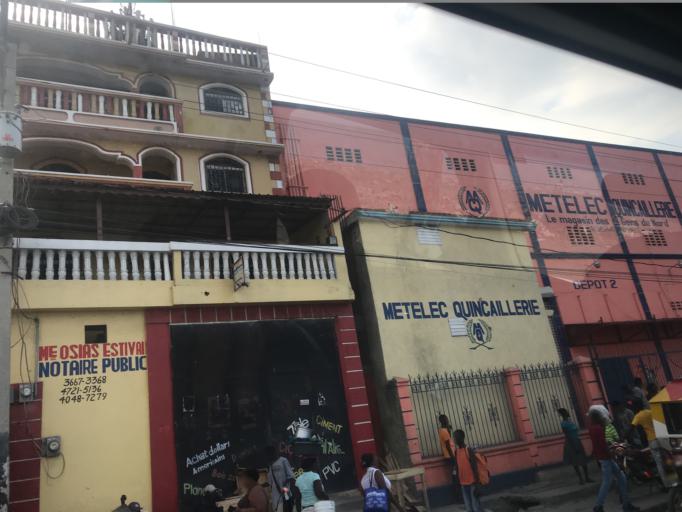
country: HT
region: Nord
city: Okap
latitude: 19.7491
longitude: -72.2023
